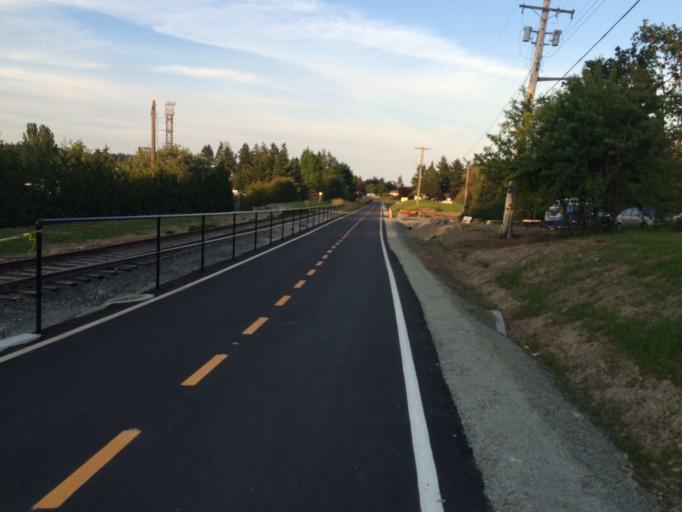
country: CA
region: British Columbia
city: Colwood
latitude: 48.4604
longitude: -123.4480
